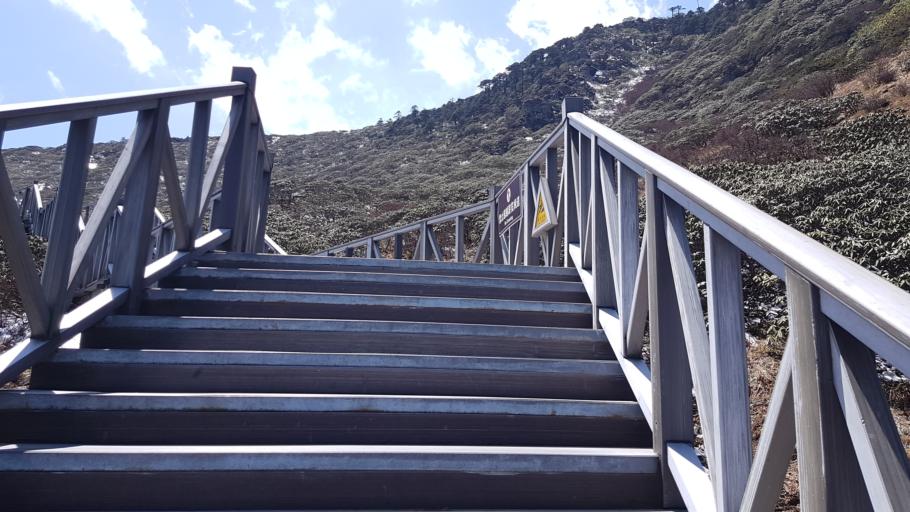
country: CN
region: Yunnan
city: Shangjie
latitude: 25.6610
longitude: 100.0996
